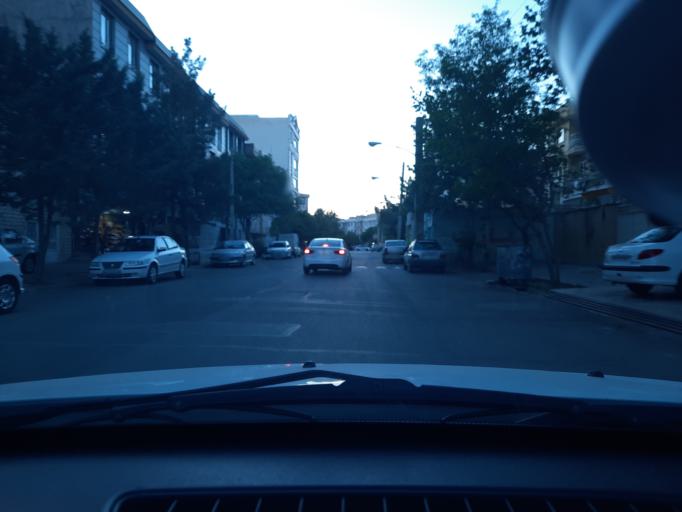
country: IR
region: Qazvin
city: Qazvin
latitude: 36.2982
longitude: 50.0169
